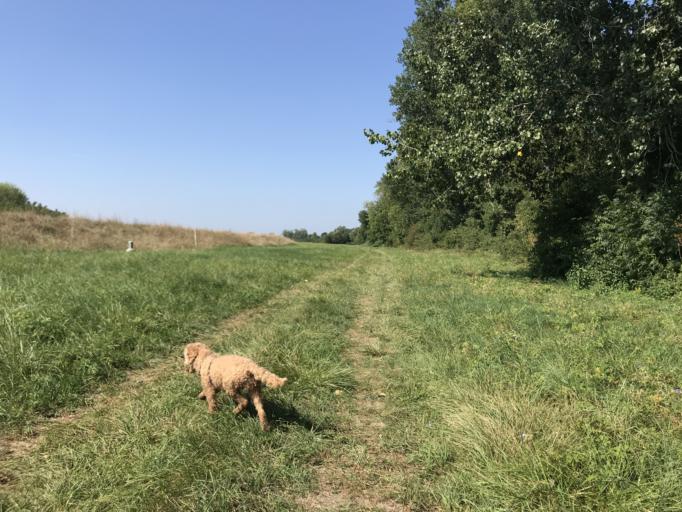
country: DE
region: Hesse
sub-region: Regierungsbezirk Darmstadt
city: Bischofsheim
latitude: 49.9996
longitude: 8.3800
